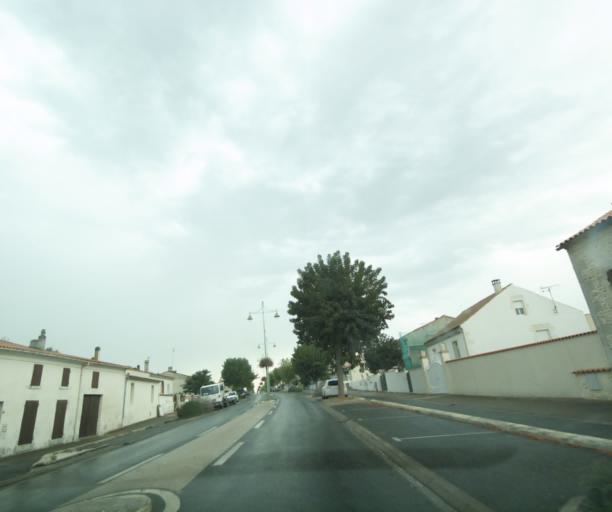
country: FR
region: Poitou-Charentes
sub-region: Departement de la Charente-Maritime
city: Tonnay-Charente
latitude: 45.9459
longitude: -0.8987
